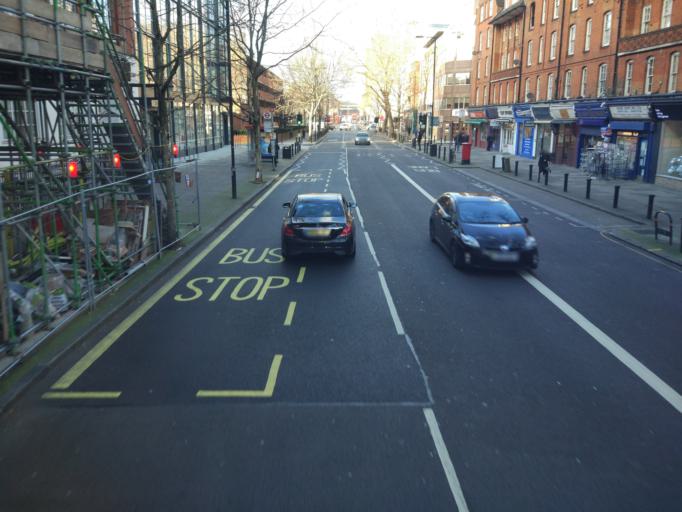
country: GB
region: England
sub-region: Greater London
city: Lambeth
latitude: 51.4995
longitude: -0.1067
